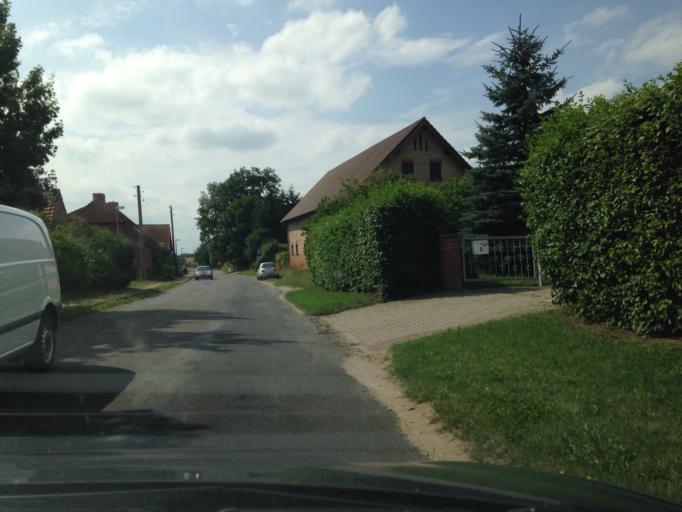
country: DE
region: Mecklenburg-Vorpommern
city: Loitz
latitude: 53.3238
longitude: 13.4143
